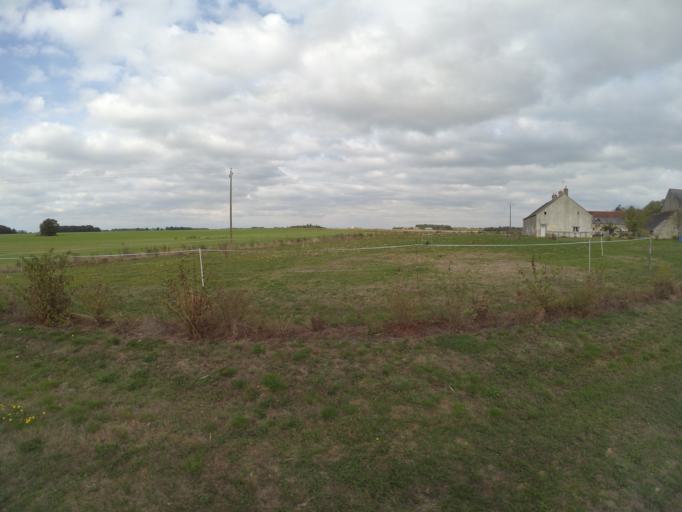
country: FR
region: Centre
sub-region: Departement d'Indre-et-Loire
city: Nazelles-Negron
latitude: 47.4699
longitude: 0.9371
